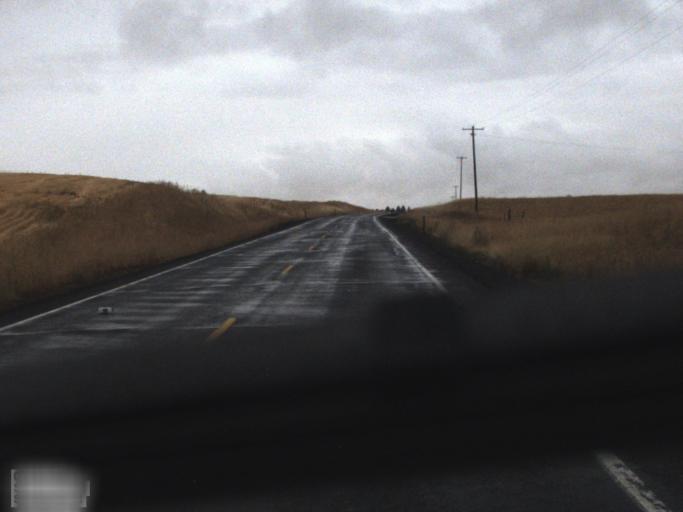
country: US
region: Washington
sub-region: Lincoln County
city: Davenport
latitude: 47.4781
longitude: -118.2058
